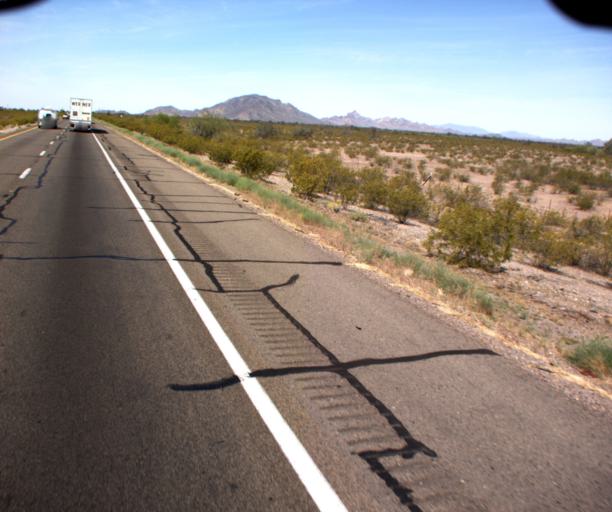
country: US
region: Arizona
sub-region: Maricopa County
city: Buckeye
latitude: 33.5052
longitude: -112.9772
